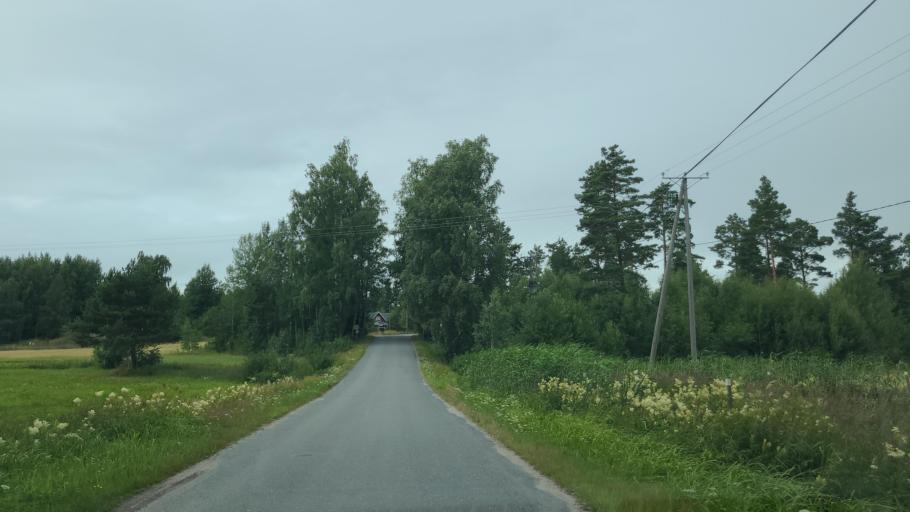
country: FI
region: Varsinais-Suomi
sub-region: Aboland-Turunmaa
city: Dragsfjaerd
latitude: 60.0971
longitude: 22.4334
